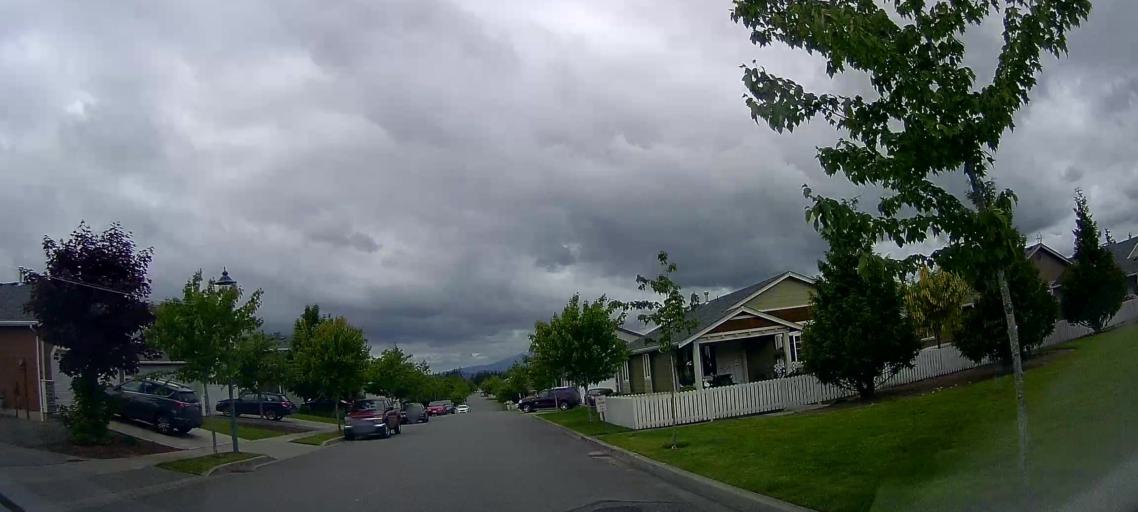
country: US
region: Washington
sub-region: Skagit County
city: Big Lake
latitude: 48.4147
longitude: -122.2830
